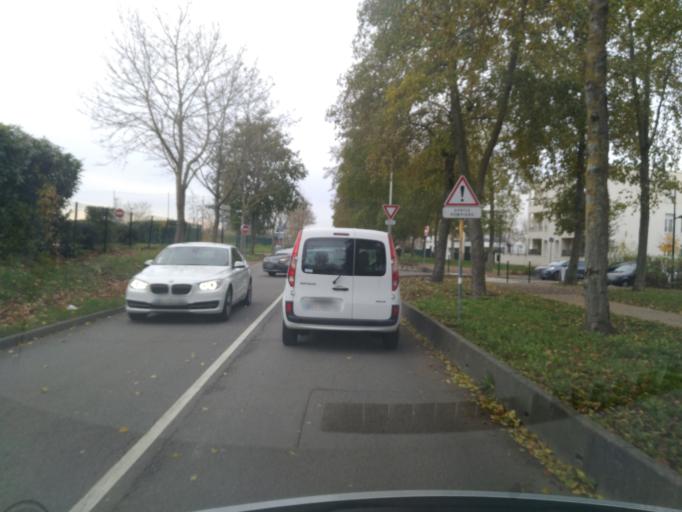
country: FR
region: Ile-de-France
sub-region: Departement des Yvelines
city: Plaisir
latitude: 48.8187
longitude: 1.9608
